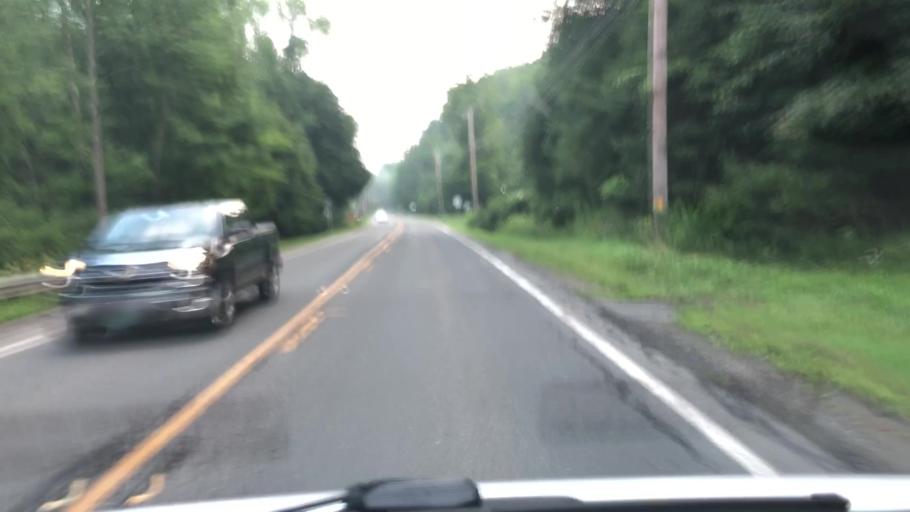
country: US
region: Massachusetts
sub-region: Berkshire County
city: Williamstown
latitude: 42.7024
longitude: -73.2226
